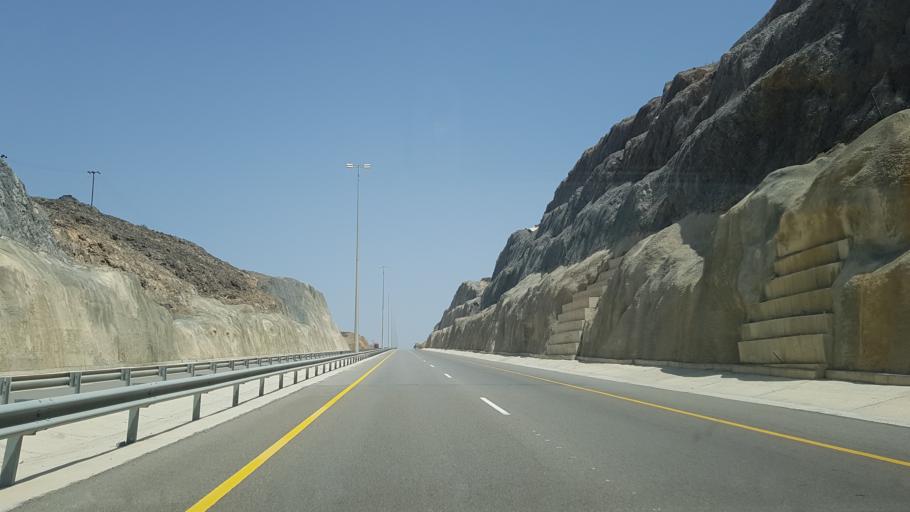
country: OM
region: Muhafazat Masqat
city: Muscat
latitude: 23.2096
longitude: 58.8056
